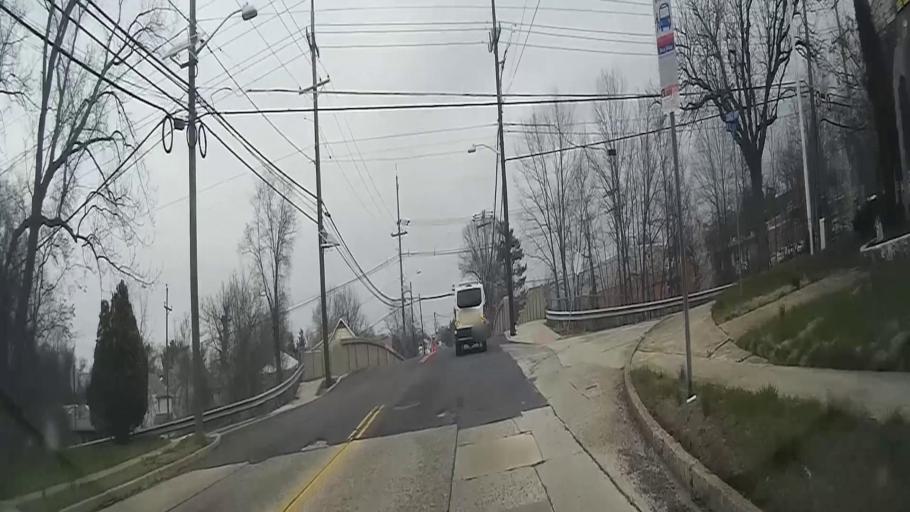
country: US
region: New Jersey
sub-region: Camden County
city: Haddon Heights
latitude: 39.8856
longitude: -75.0626
